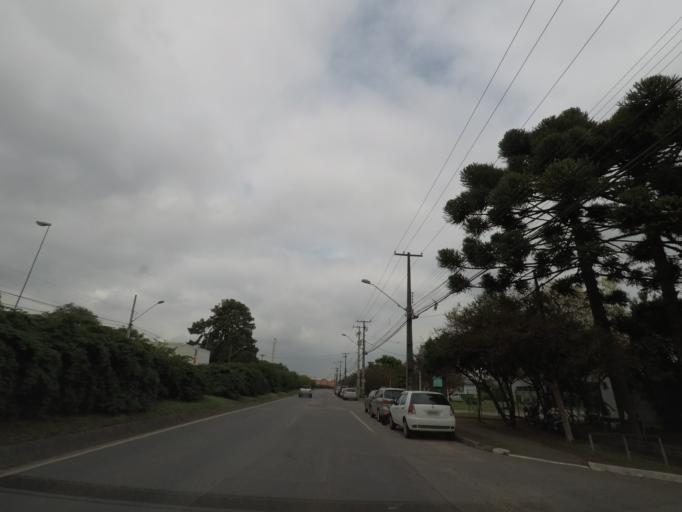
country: BR
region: Parana
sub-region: Curitiba
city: Curitiba
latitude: -25.5059
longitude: -49.3289
